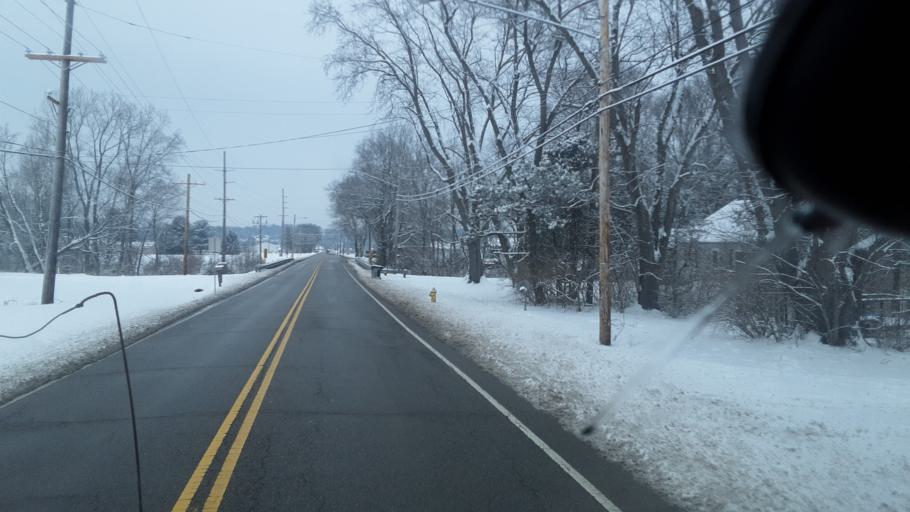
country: US
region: Ohio
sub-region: Licking County
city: Heath
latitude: 40.0247
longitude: -82.4801
